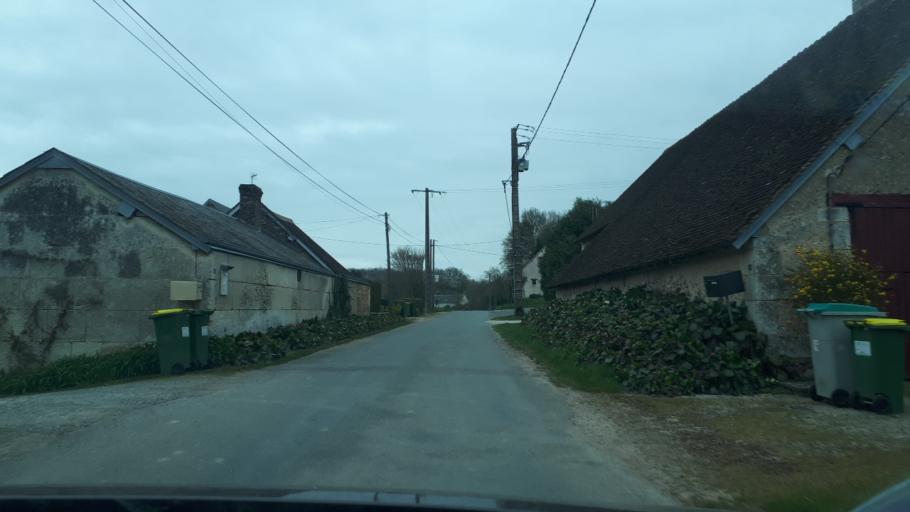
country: FR
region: Centre
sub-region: Departement du Loir-et-Cher
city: Lunay
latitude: 47.7497
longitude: 0.9405
